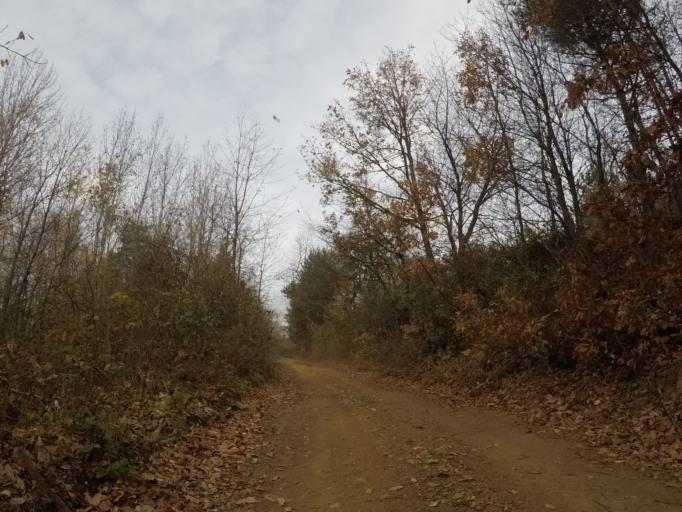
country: SK
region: Presovsky
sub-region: Okres Presov
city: Presov
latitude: 48.9232
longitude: 21.1441
